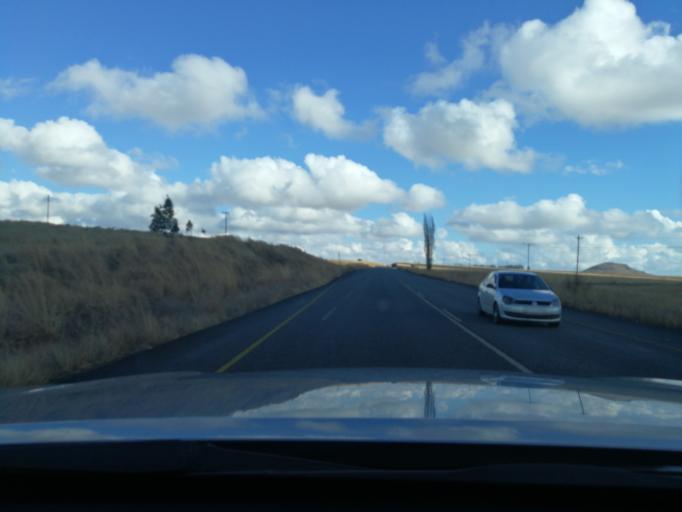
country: ZA
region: Orange Free State
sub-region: Thabo Mofutsanyana District Municipality
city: Reitz
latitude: -27.9554
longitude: 28.3819
